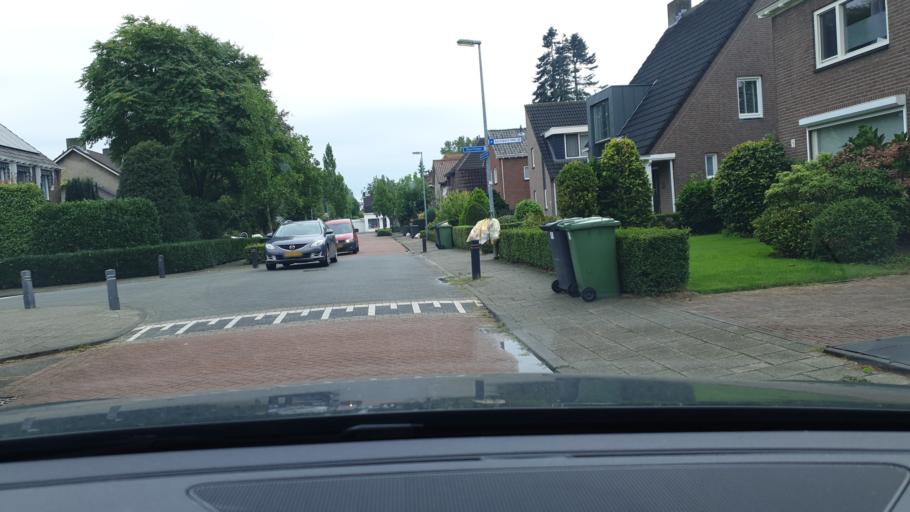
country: NL
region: North Brabant
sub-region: Gemeente Veldhoven
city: Veldhoven
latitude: 51.4199
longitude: 5.4128
